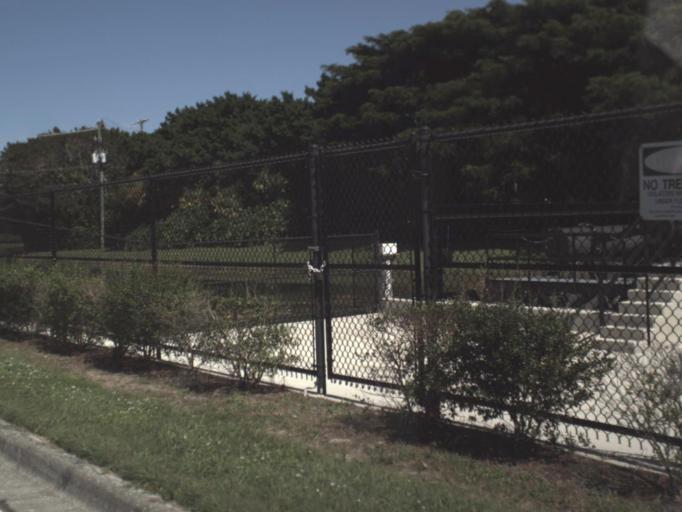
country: US
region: Florida
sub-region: Collier County
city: Naples
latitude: 26.1815
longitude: -81.7673
